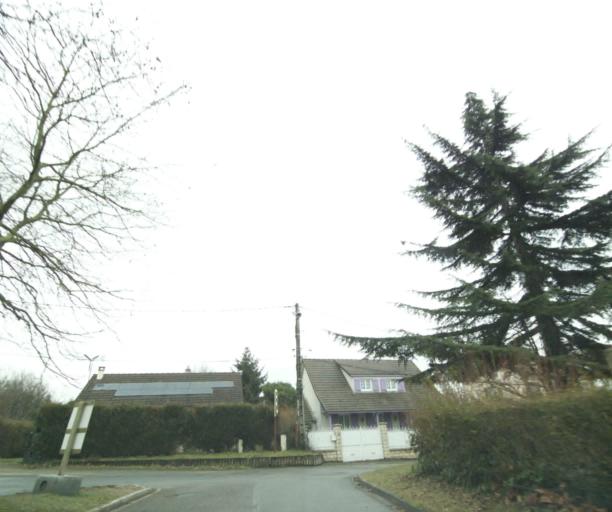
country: FR
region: Ile-de-France
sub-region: Departement de l'Essonne
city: Champlan
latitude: 48.7117
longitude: 2.2744
